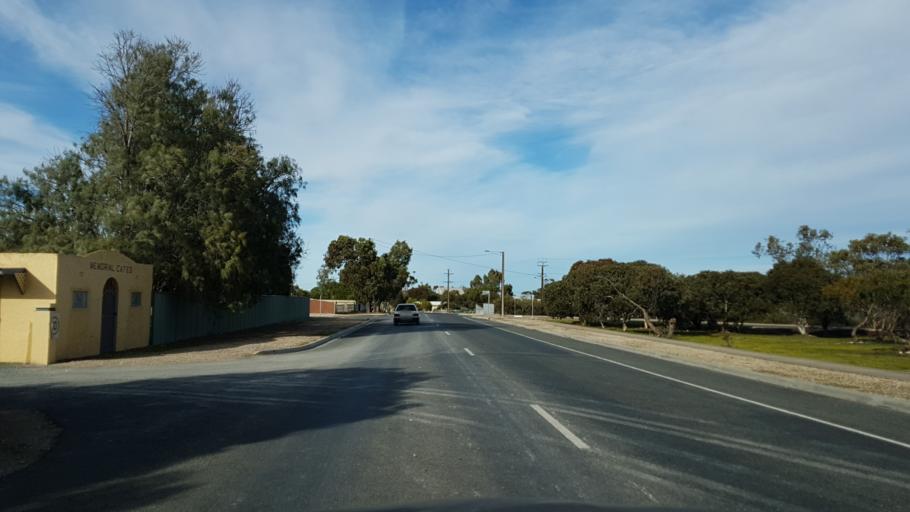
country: AU
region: South Australia
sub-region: Murray Bridge
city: Tailem Bend
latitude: -35.2489
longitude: 139.4551
